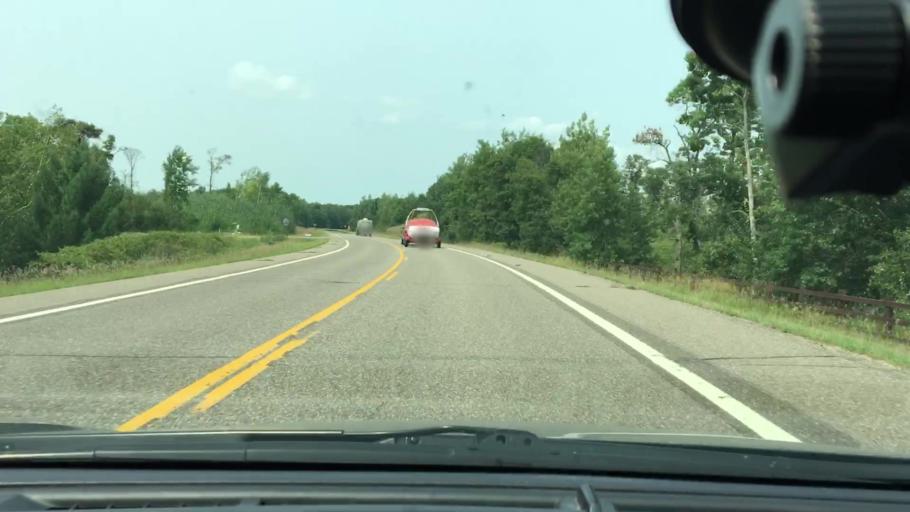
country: US
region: Minnesota
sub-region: Cass County
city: East Gull Lake
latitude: 46.4025
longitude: -94.3512
